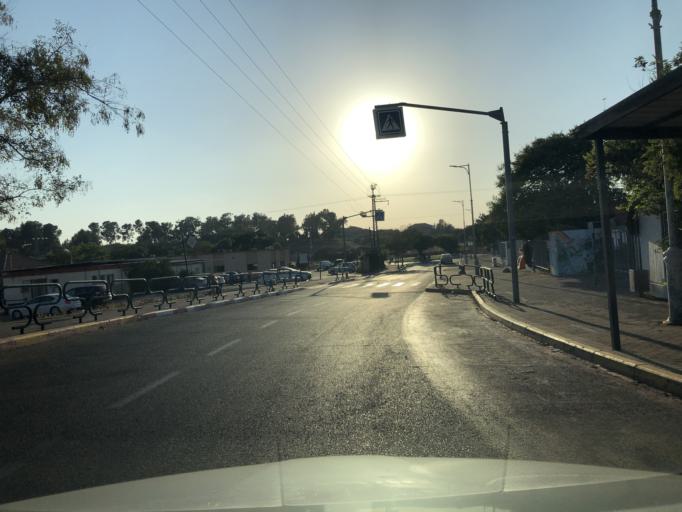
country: PS
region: West Bank
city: Hablah
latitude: 32.1555
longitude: 34.9746
